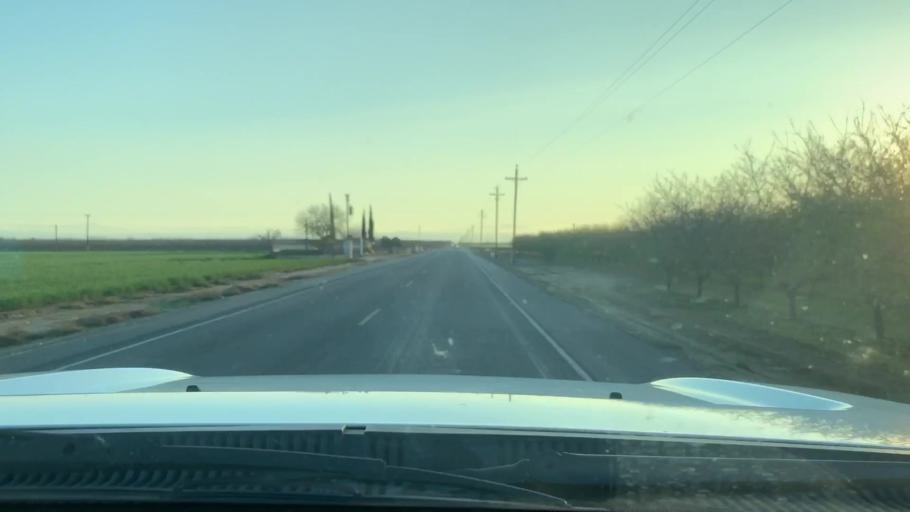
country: US
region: California
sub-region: Kern County
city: Wasco
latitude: 35.5001
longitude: -119.3703
